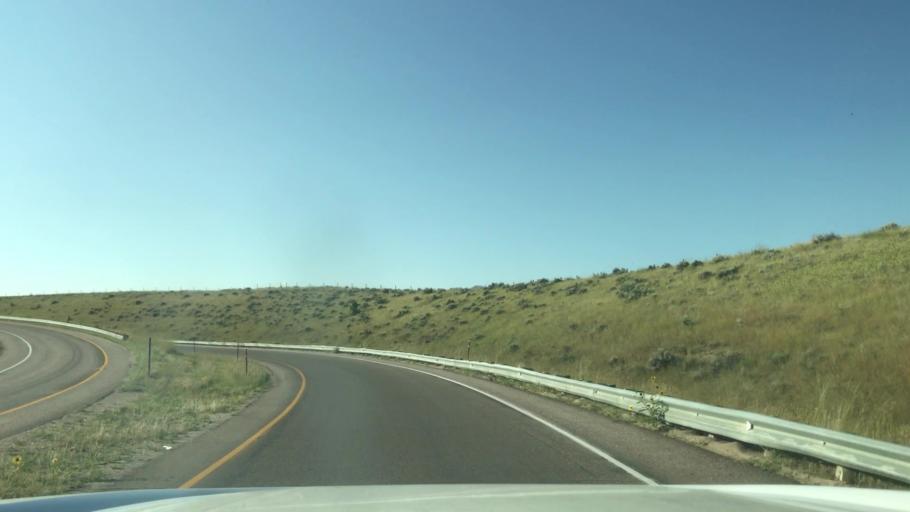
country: US
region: Wyoming
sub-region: Converse County
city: Douglas
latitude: 42.7308
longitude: -105.3413
